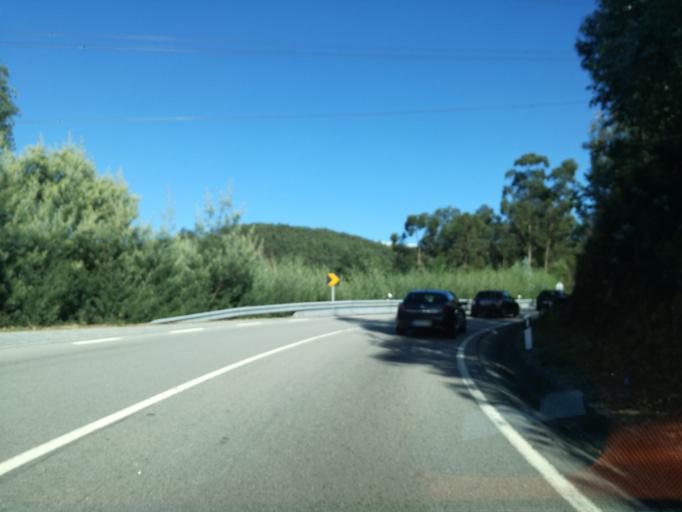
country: PT
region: Porto
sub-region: Pacos de Ferreira
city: Seroa
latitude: 41.2614
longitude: -8.4603
